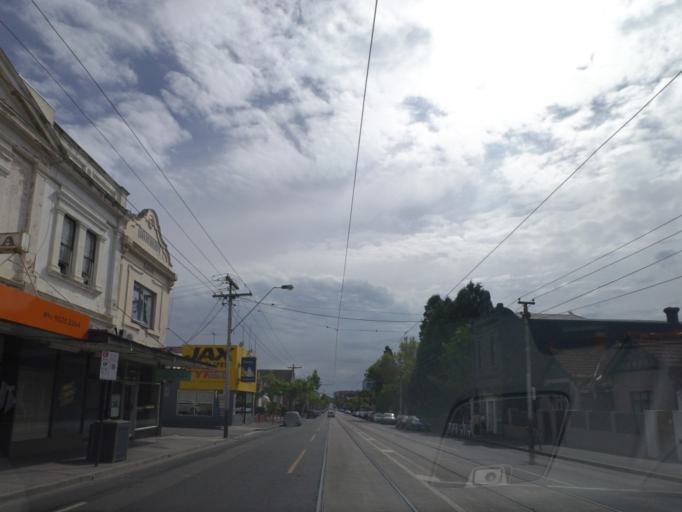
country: AU
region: Victoria
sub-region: Stonnington
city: Windsor
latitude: -37.8530
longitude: 145.0015
